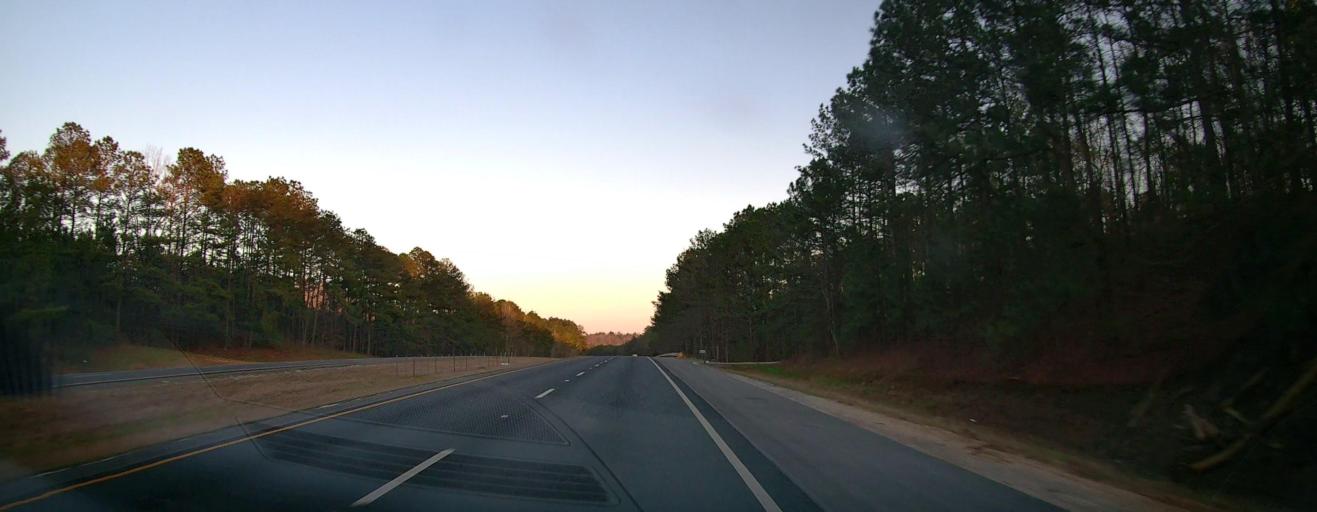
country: US
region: Alabama
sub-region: Coosa County
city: Stewartville
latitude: 33.0786
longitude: -86.1856
